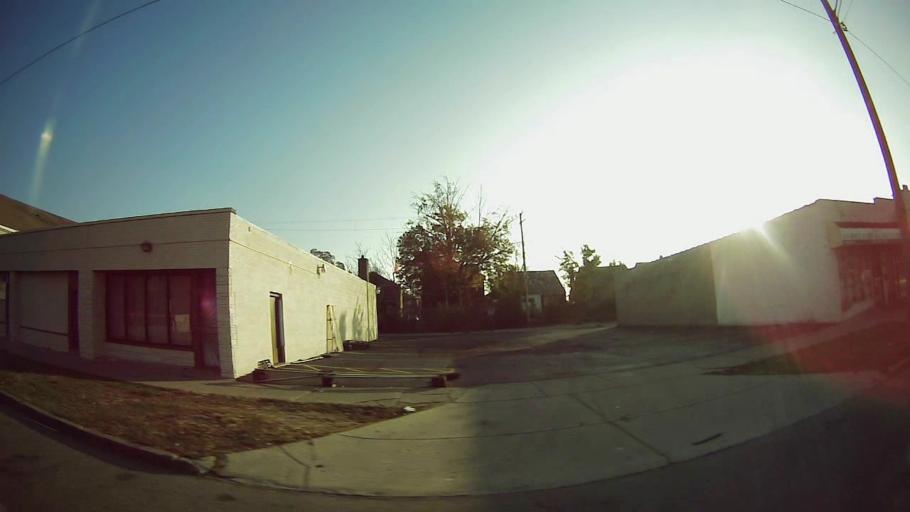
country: US
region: Michigan
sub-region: Oakland County
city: Oak Park
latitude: 42.4264
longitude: -83.1607
